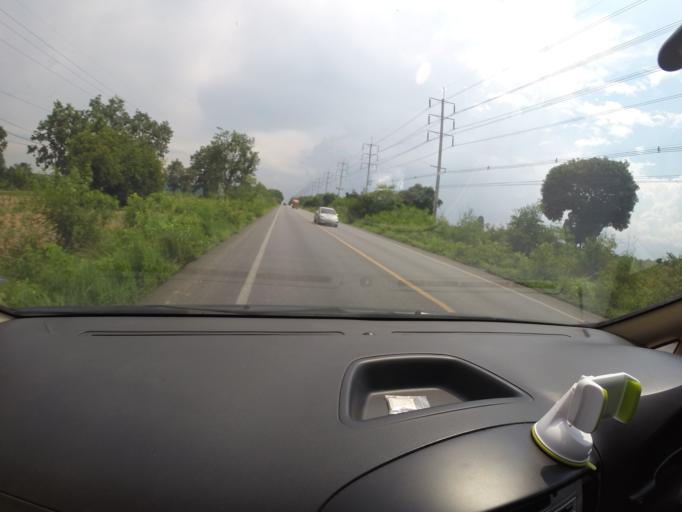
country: TH
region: Lop Buri
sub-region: Amphoe Lam Sonthi
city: Lam Sonthi
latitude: 15.1105
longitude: 101.4601
